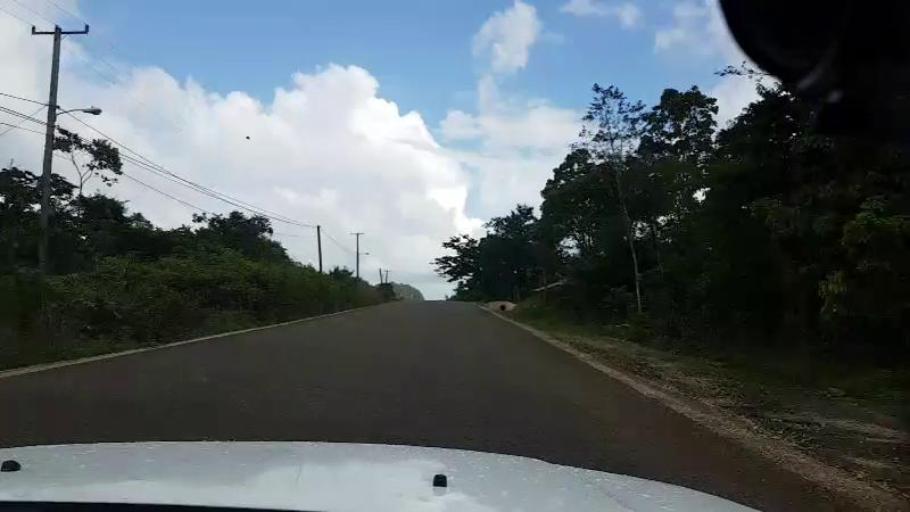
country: BZ
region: Cayo
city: Belmopan
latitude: 17.0918
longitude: -88.6384
